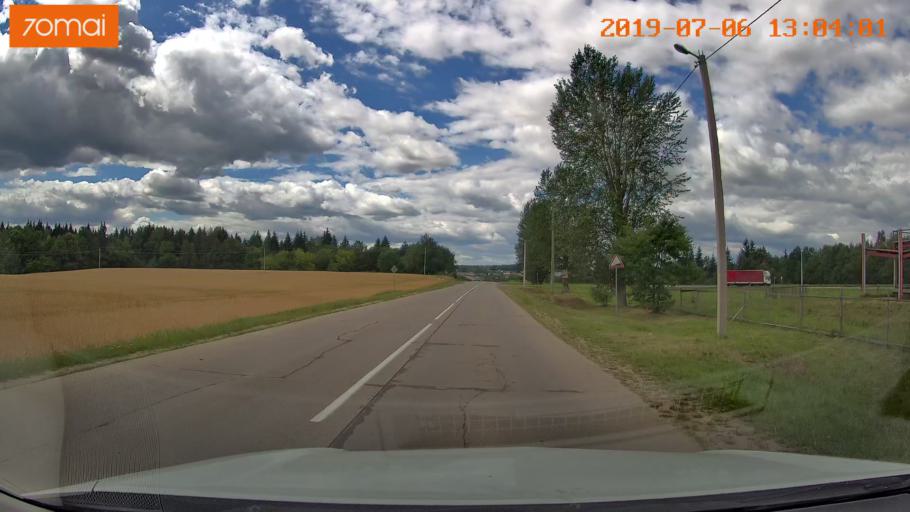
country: BY
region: Minsk
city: Dzyarzhynsk
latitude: 53.6905
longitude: 27.0921
